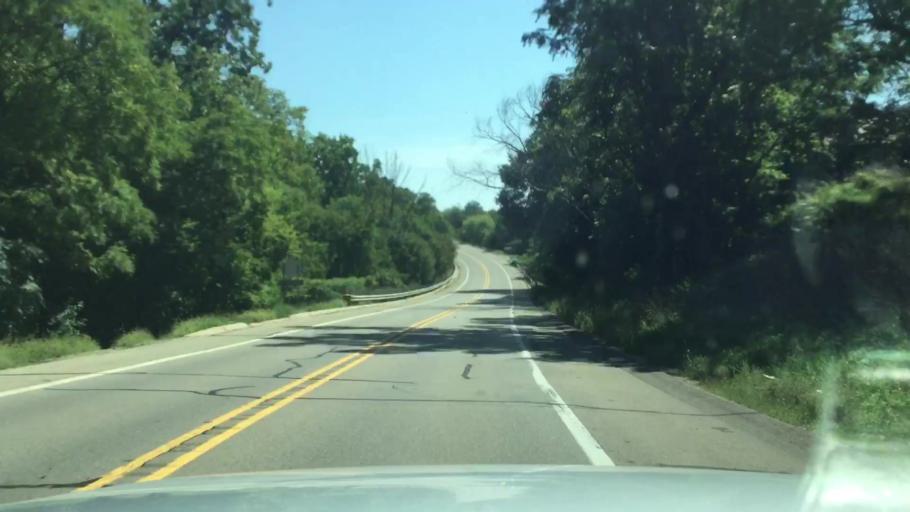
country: US
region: Michigan
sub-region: Jackson County
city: Brooklyn
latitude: 42.0590
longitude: -84.1780
